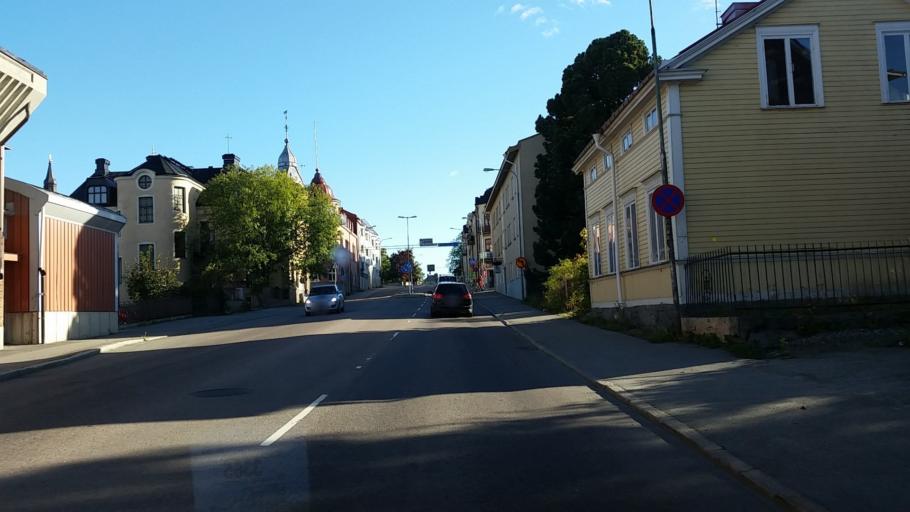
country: SE
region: Gaevleborg
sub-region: Hudiksvalls Kommun
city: Hudiksvall
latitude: 61.7281
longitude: 17.1013
